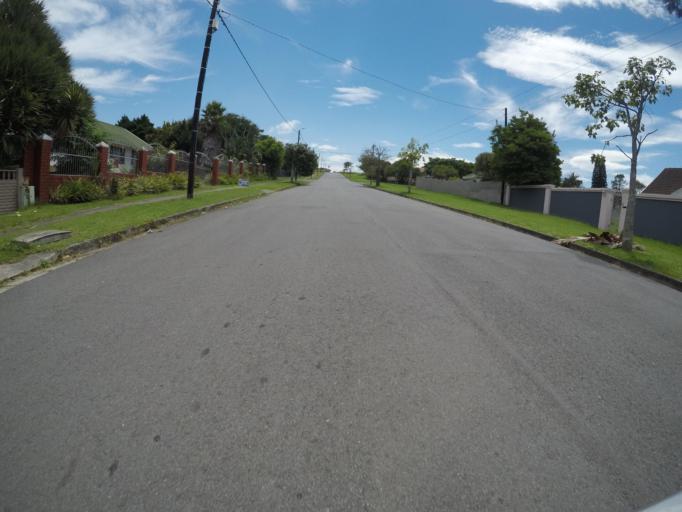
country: ZA
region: Eastern Cape
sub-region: Buffalo City Metropolitan Municipality
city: East London
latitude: -33.0420
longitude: 27.8566
